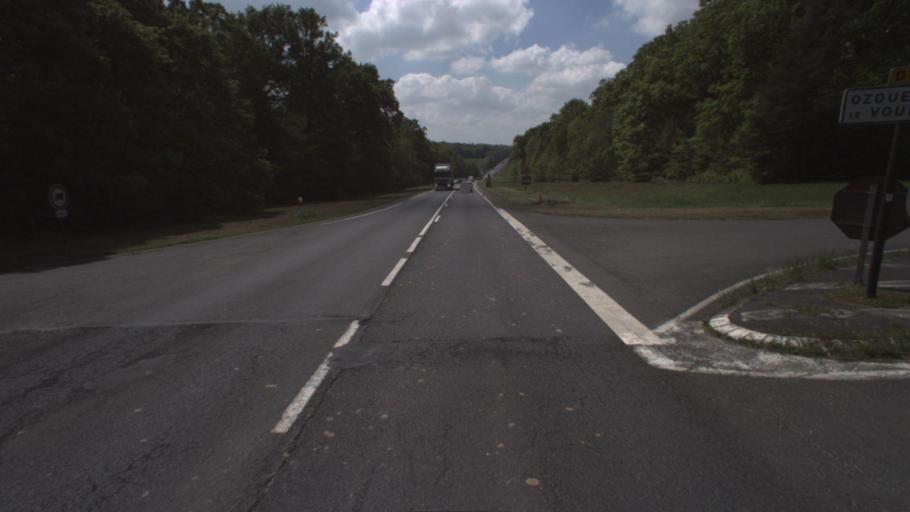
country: FR
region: Ile-de-France
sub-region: Departement de Seine-et-Marne
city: Chaumes-en-Brie
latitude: 48.6647
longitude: 2.8106
